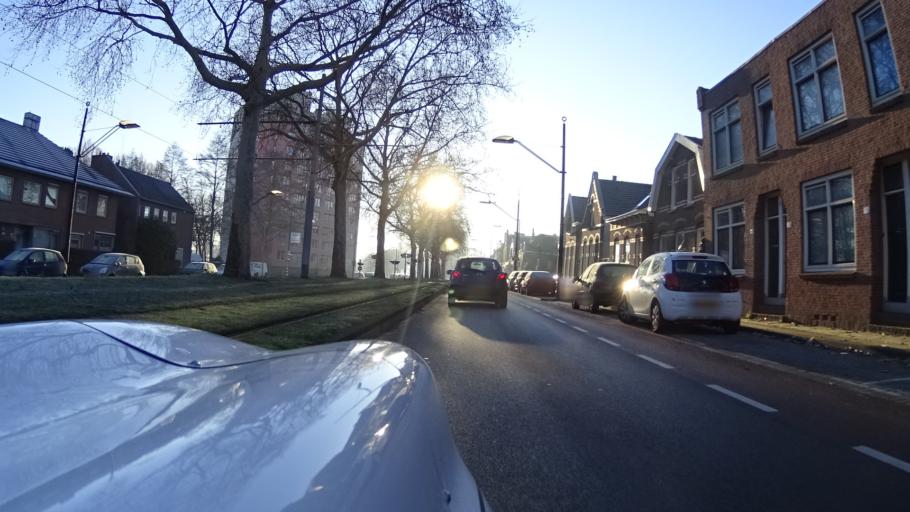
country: NL
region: South Holland
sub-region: Gemeente Barendrecht
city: Barendrecht
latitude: 51.8809
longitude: 4.5060
